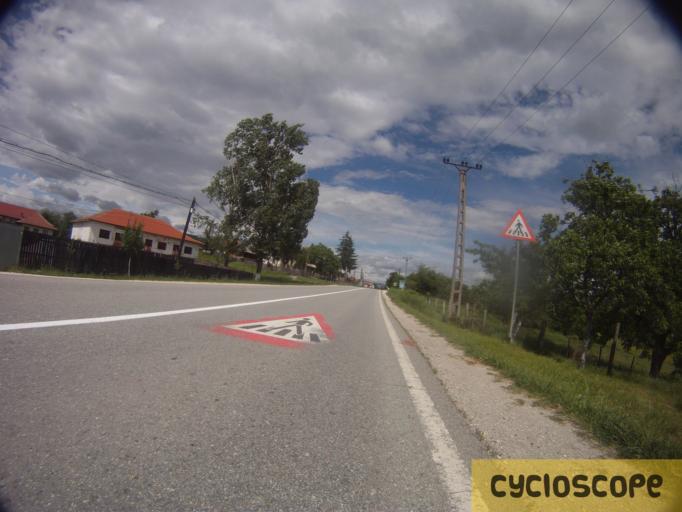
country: RO
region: Gorj
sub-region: Comuna Bengesti-Ciocadia
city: Balcesti
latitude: 45.1075
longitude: 23.6422
